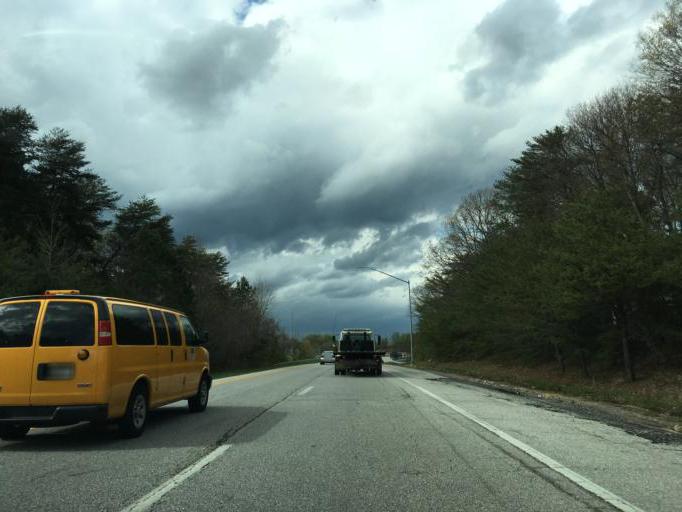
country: US
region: Maryland
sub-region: Anne Arundel County
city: Ferndale
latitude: 39.1686
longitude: -76.6391
